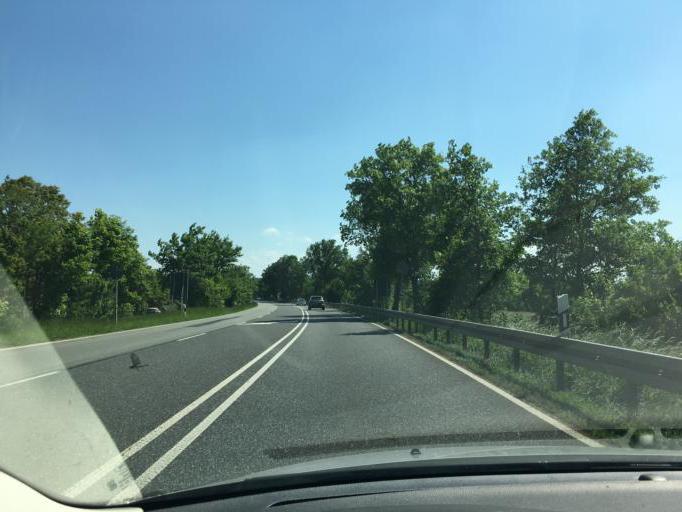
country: DE
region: Hesse
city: Breitenbach
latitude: 50.9673
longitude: 9.7822
